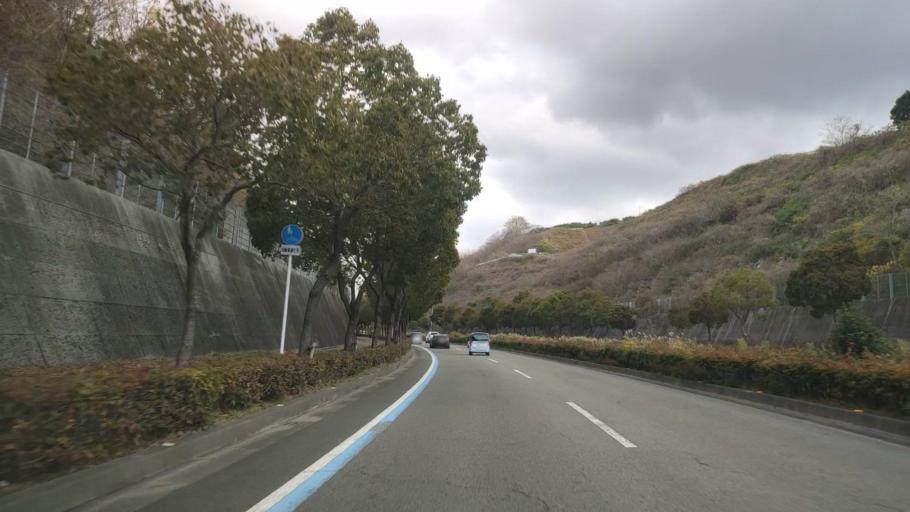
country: JP
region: Ehime
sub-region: Shikoku-chuo Shi
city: Matsuyama
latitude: 33.8877
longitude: 132.7550
